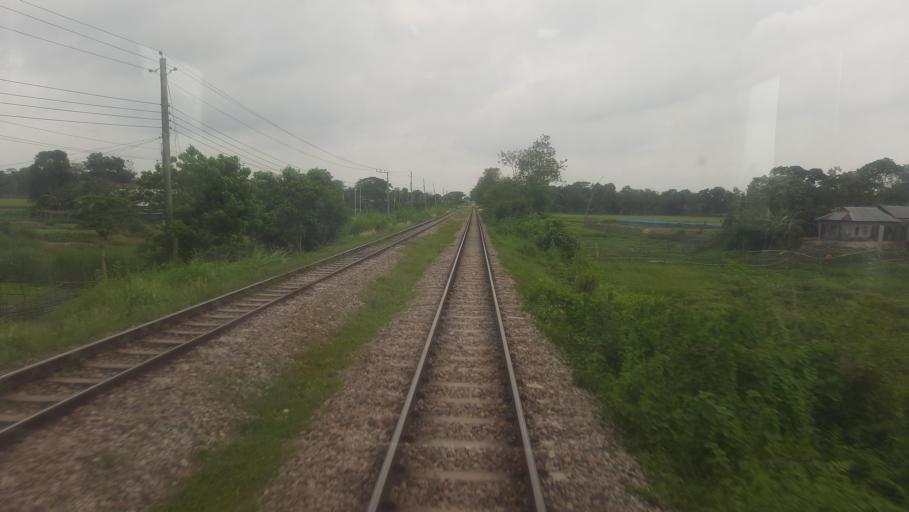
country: BD
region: Dhaka
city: Bhairab Bazar
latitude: 23.9819
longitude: 91.0755
